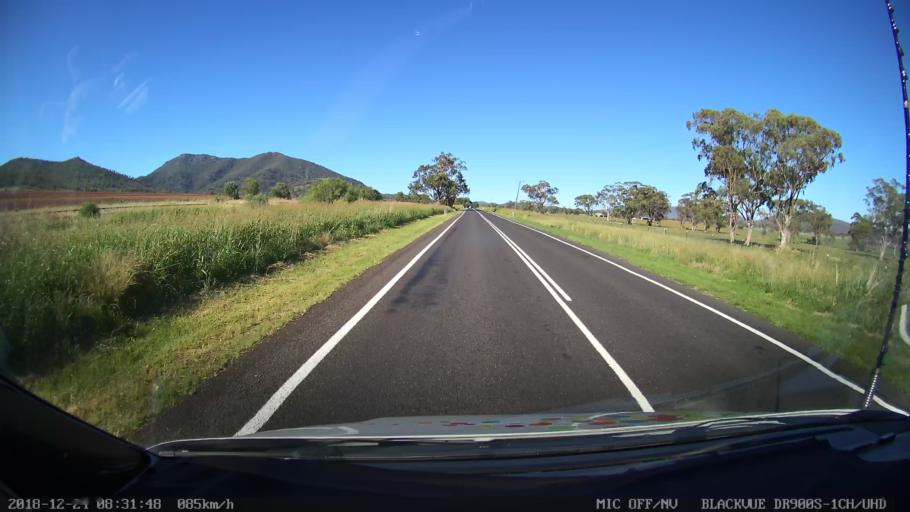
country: AU
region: New South Wales
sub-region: Tamworth Municipality
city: Phillip
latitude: -31.2759
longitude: 150.7065
